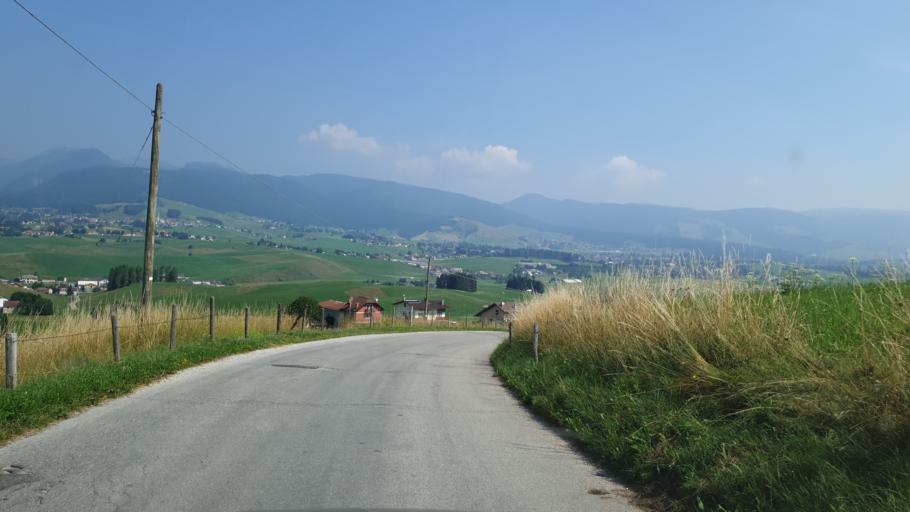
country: IT
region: Veneto
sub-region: Provincia di Vicenza
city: Canove di Roana
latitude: 45.8488
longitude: 11.4924
